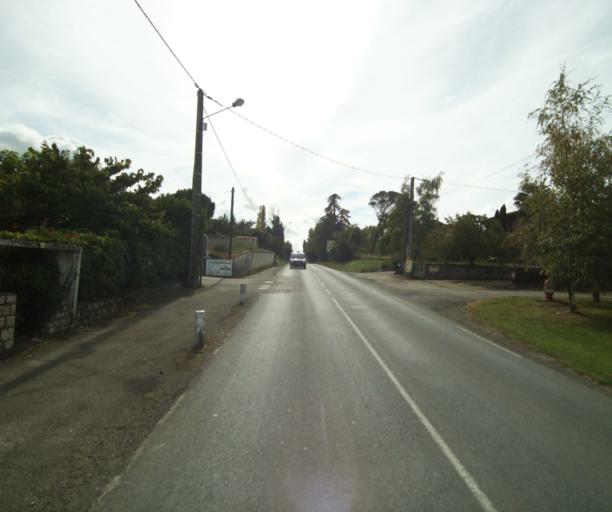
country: FR
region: Midi-Pyrenees
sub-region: Departement du Gers
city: Eauze
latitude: 43.8545
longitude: 0.0981
